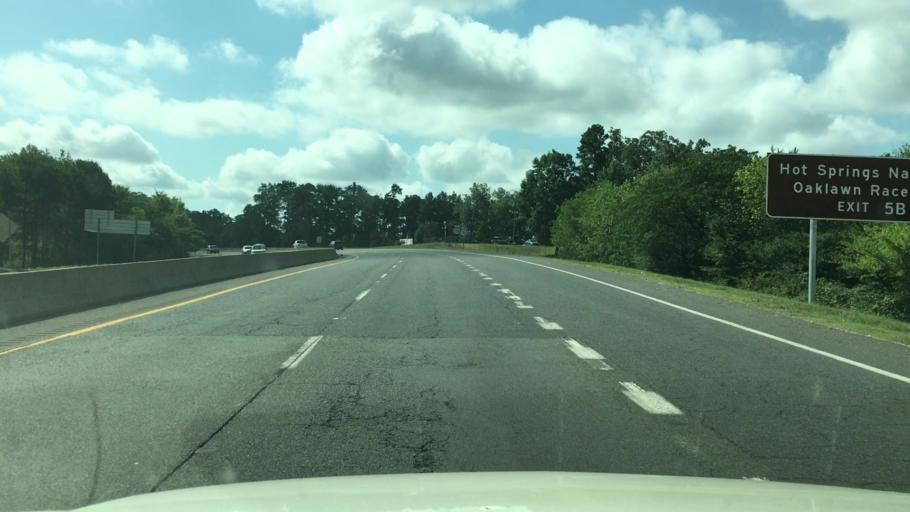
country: US
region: Arkansas
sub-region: Garland County
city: Lake Hamilton
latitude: 34.4678
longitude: -93.0879
